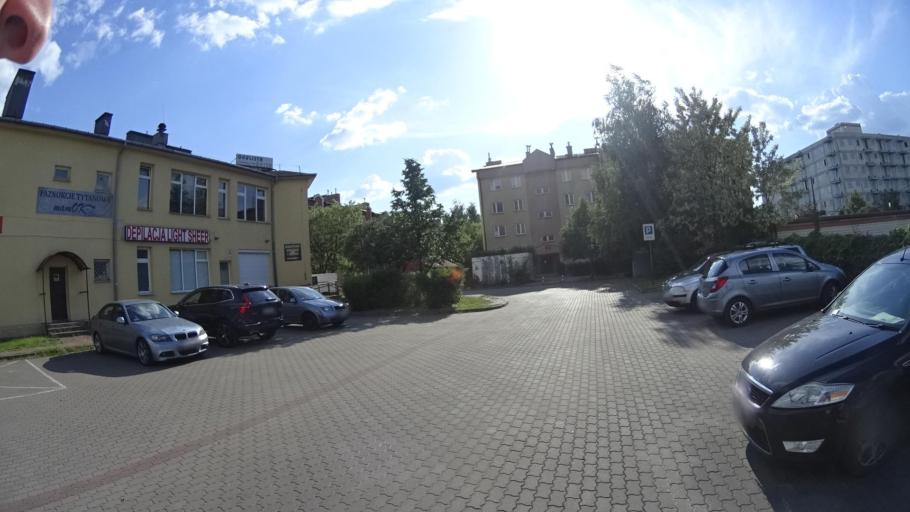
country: PL
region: Masovian Voivodeship
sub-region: Powiat pruszkowski
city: Granica
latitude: 52.1524
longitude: 20.7939
